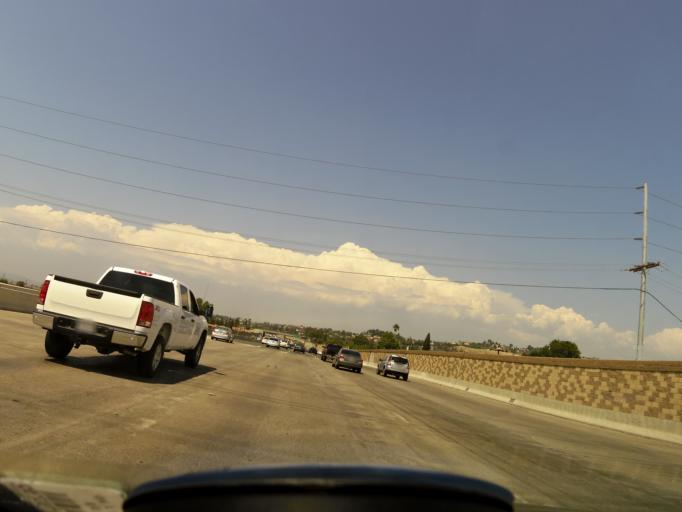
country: US
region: California
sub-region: Orange County
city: Villa Park
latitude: 33.8172
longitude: -117.8319
